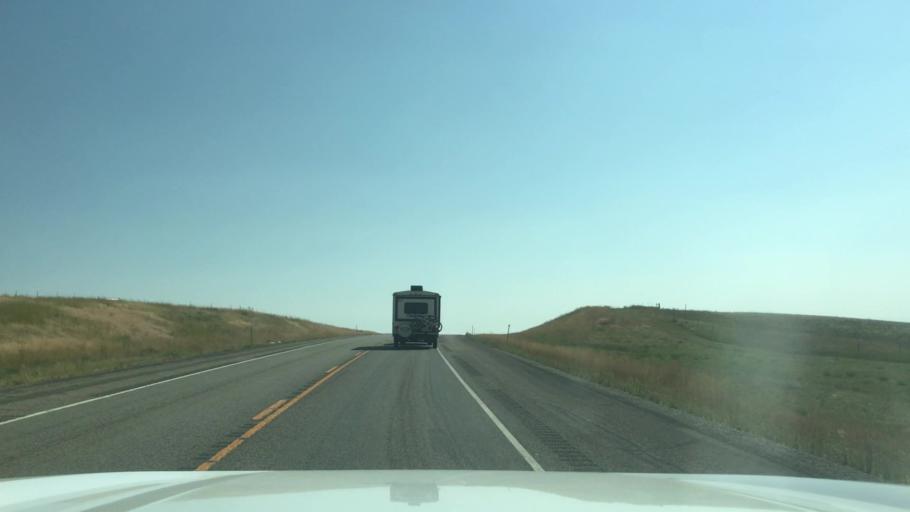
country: US
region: Montana
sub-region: Wheatland County
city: Harlowton
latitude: 46.4700
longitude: -109.7672
